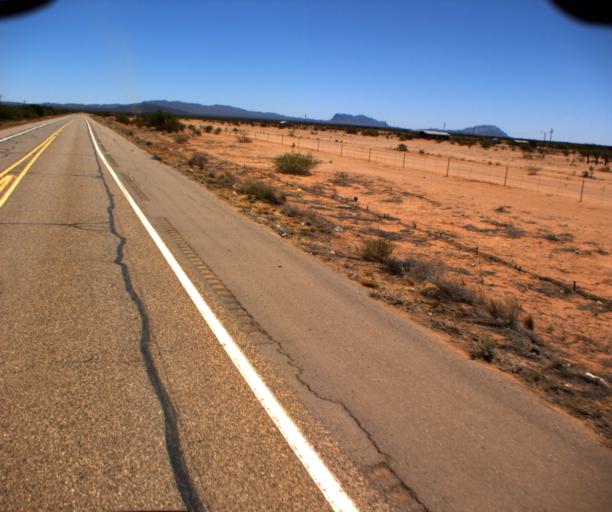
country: US
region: Arizona
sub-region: Pima County
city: Ajo
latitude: 32.1847
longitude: -112.3653
